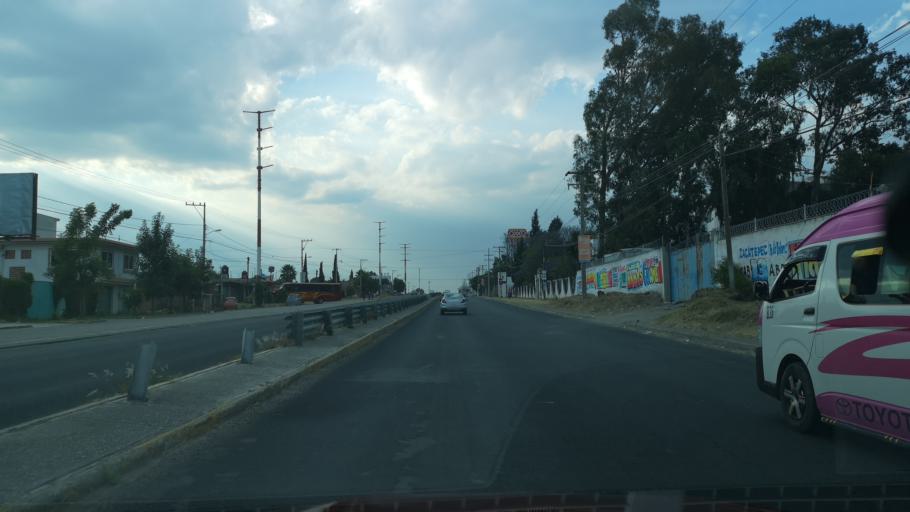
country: MX
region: Puebla
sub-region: Juan C. Bonilla
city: Santa Maria Zacatepec
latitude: 19.1110
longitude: -98.3545
